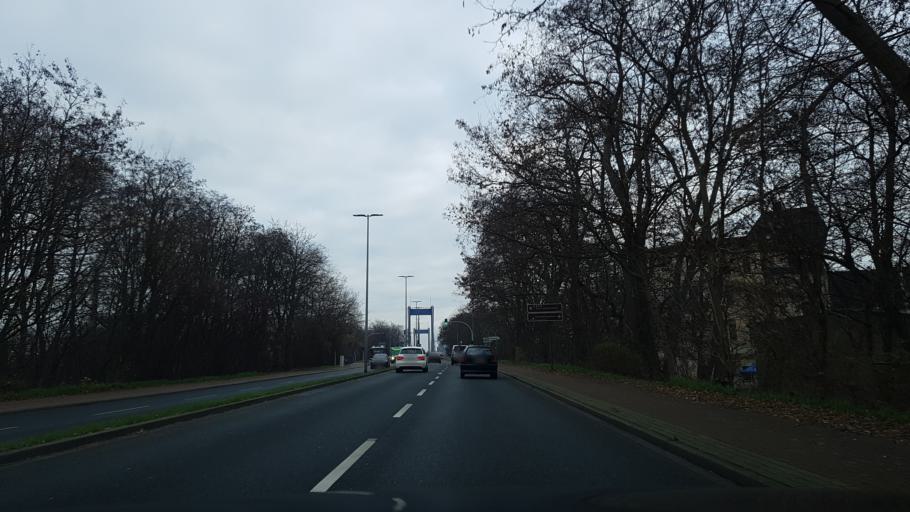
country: DE
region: North Rhine-Westphalia
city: Meiderich
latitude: 51.4569
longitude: 6.7146
